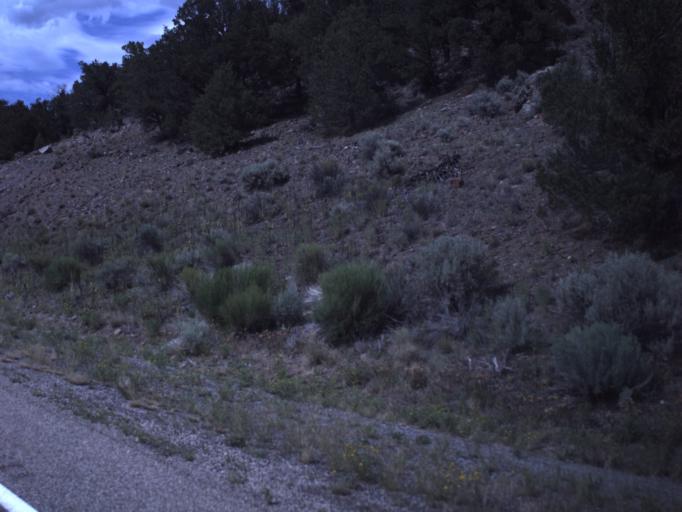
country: US
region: Utah
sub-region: Garfield County
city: Panguitch
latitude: 37.9758
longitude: -112.4832
